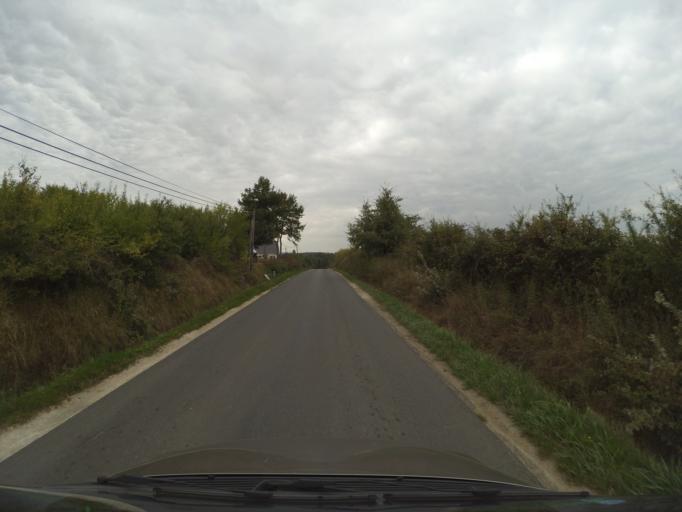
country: FR
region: Centre
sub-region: Departement d'Indre-et-Loire
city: Auzouer-en-Touraine
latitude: 47.5090
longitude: 0.9197
